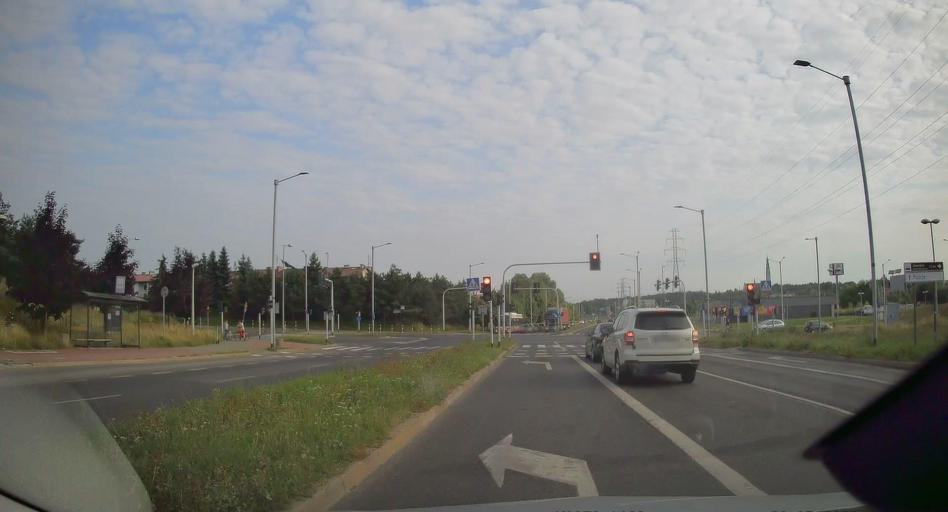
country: PL
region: Silesian Voivodeship
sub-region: Czestochowa
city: Czestochowa
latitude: 50.8252
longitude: 19.1040
